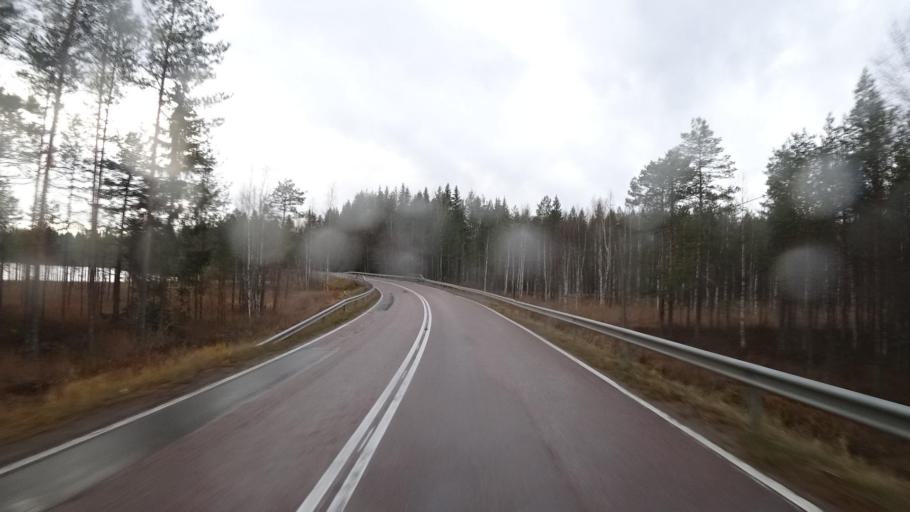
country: FI
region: Southern Savonia
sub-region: Mikkeli
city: Kangasniemi
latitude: 62.0895
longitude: 26.6991
